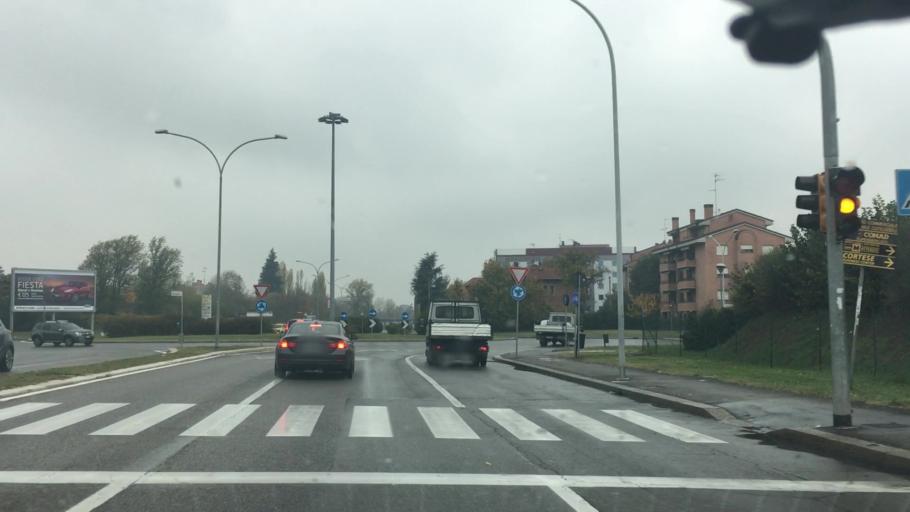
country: IT
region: Emilia-Romagna
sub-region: Provincia di Bologna
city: Casalecchio di Reno
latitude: 44.5070
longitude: 11.2842
